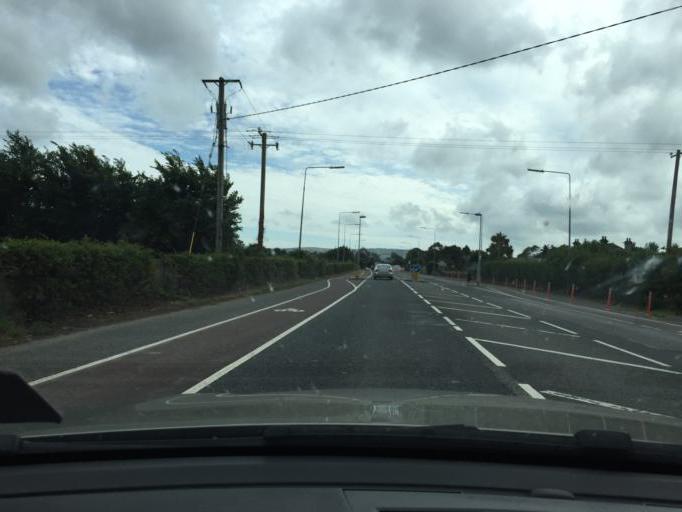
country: IE
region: Munster
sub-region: Waterford
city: Dungarvan
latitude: 52.1017
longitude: -7.6062
